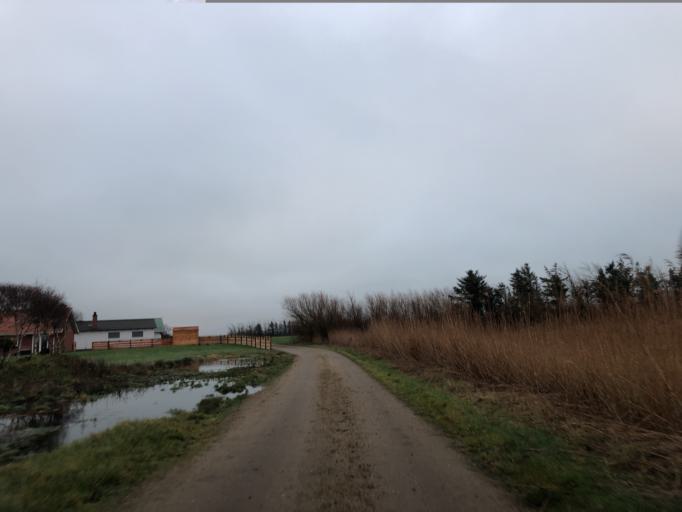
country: DK
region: Central Jutland
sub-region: Ringkobing-Skjern Kommune
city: Ringkobing
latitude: 56.1503
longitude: 8.2408
